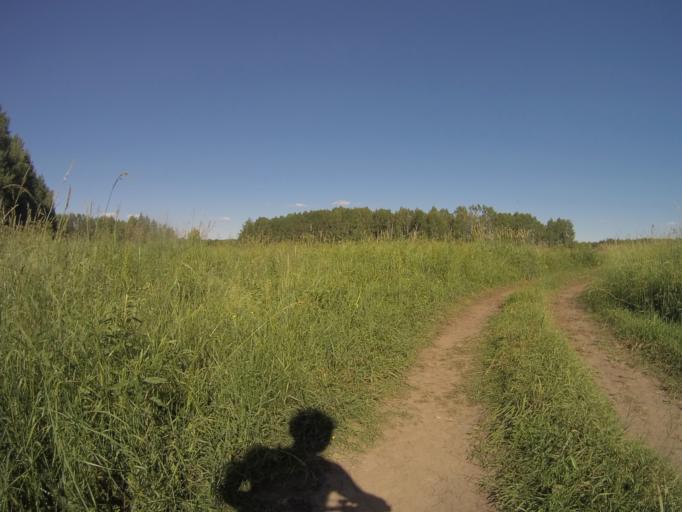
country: RU
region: Vladimir
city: Golovino
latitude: 56.0009
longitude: 40.3992
